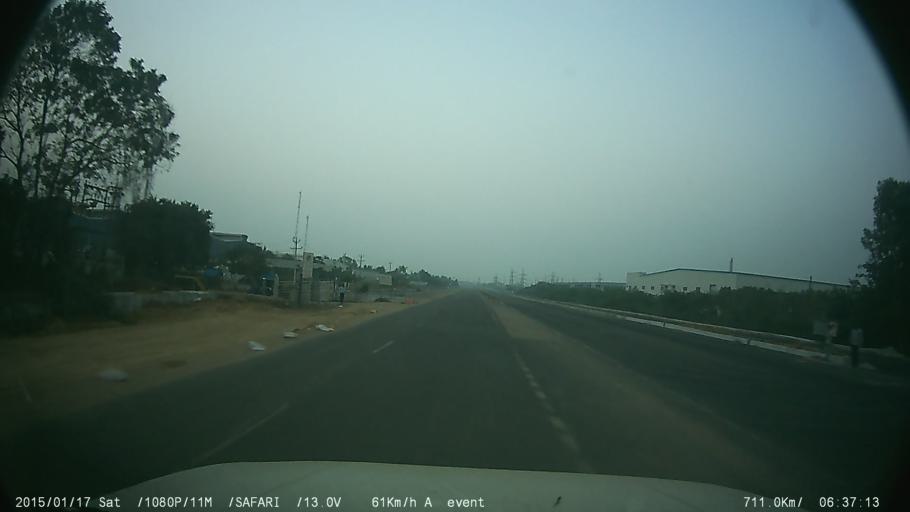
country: IN
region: Tamil Nadu
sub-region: Kancheepuram
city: Sriperumbudur
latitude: 12.9487
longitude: 79.9384
